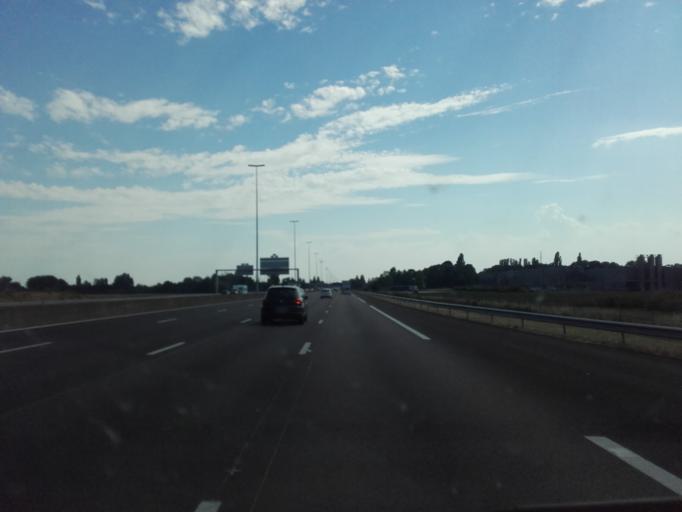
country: FR
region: Bourgogne
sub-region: Departement de la Cote-d'Or
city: Beaune
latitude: 47.0090
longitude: 4.8641
